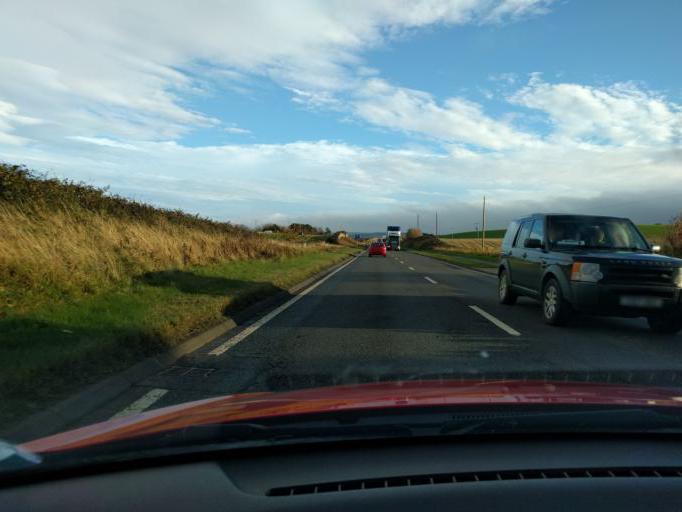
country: GB
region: Scotland
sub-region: East Lothian
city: Dunbar
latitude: 55.9587
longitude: -2.4011
